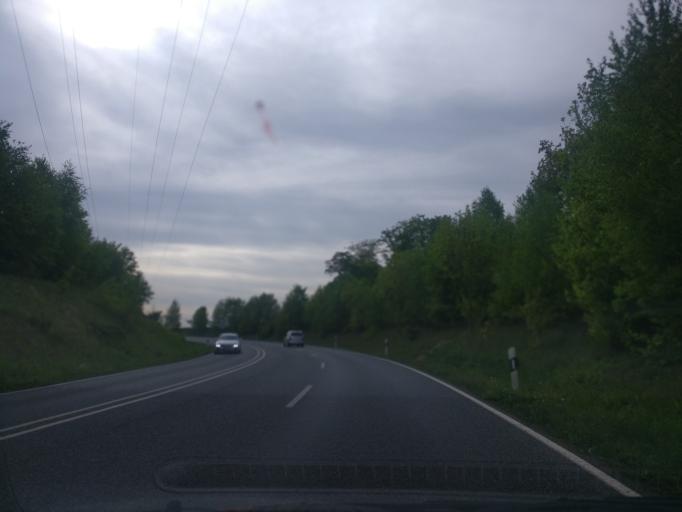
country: DE
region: Hesse
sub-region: Regierungsbezirk Kassel
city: Vellmar
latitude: 51.3611
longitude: 9.5213
